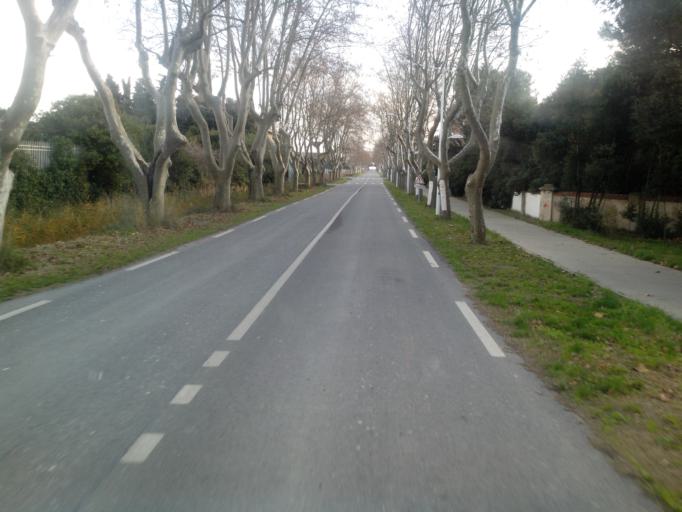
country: FR
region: Provence-Alpes-Cote d'Azur
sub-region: Departement des Bouches-du-Rhone
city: Port-Saint-Louis-du-Rhone
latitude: 43.4194
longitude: 4.7342
